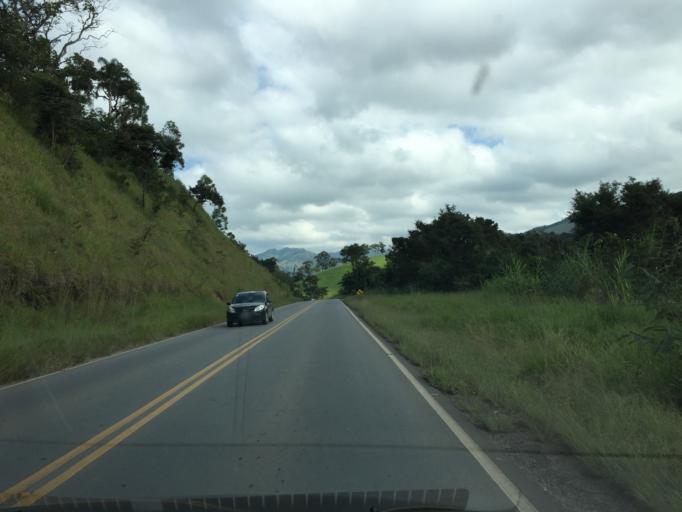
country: BR
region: Minas Gerais
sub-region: Passa Quatro
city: Passa Quatro
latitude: -22.3691
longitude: -44.9608
